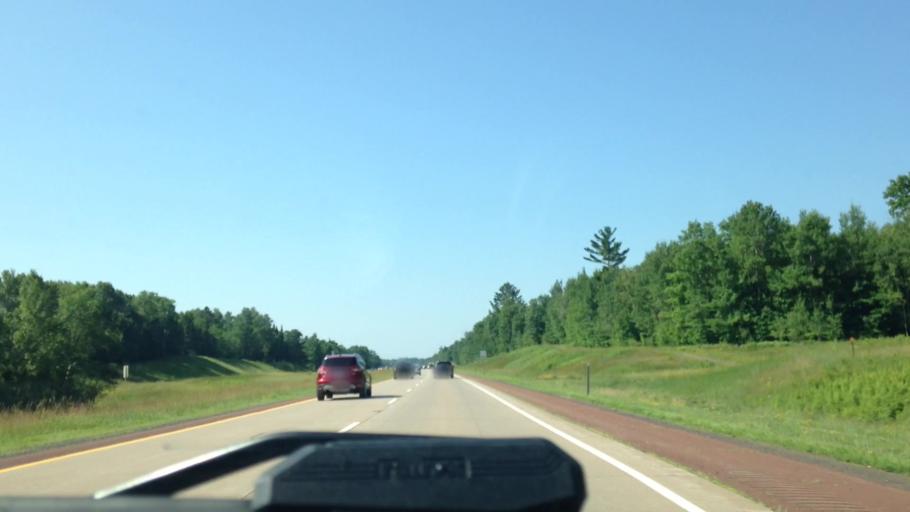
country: US
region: Wisconsin
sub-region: Douglas County
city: Lake Nebagamon
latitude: 46.3805
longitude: -91.8236
